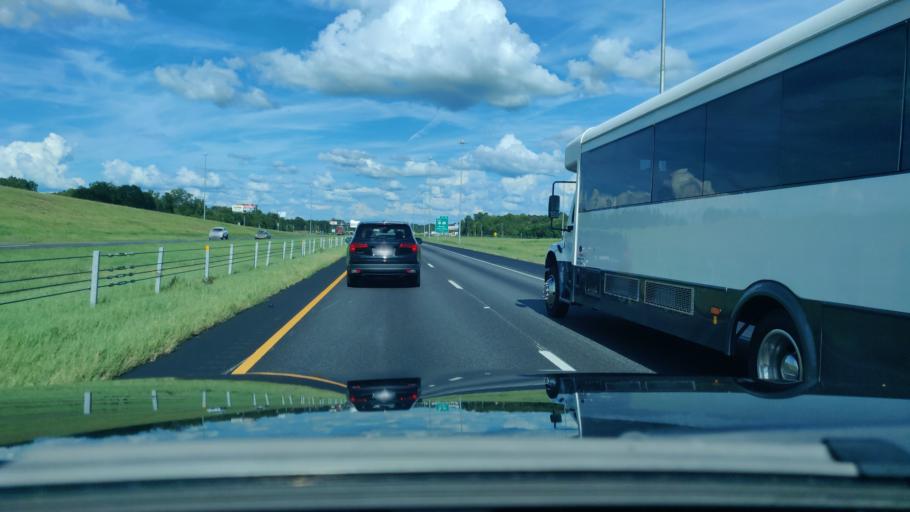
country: US
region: Alabama
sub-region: Montgomery County
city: Pike Road
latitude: 32.3683
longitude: -86.0763
